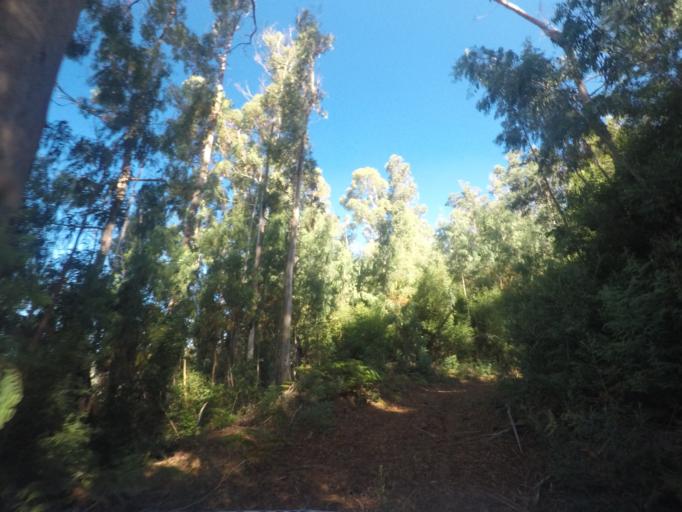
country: PT
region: Madeira
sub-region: Funchal
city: Nossa Senhora do Monte
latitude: 32.6899
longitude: -16.9130
